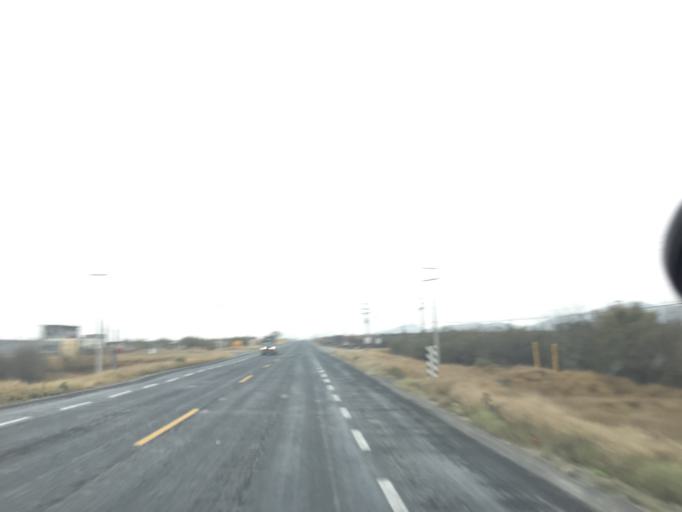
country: MX
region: Nuevo Leon
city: Mina
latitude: 25.9995
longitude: -100.4896
